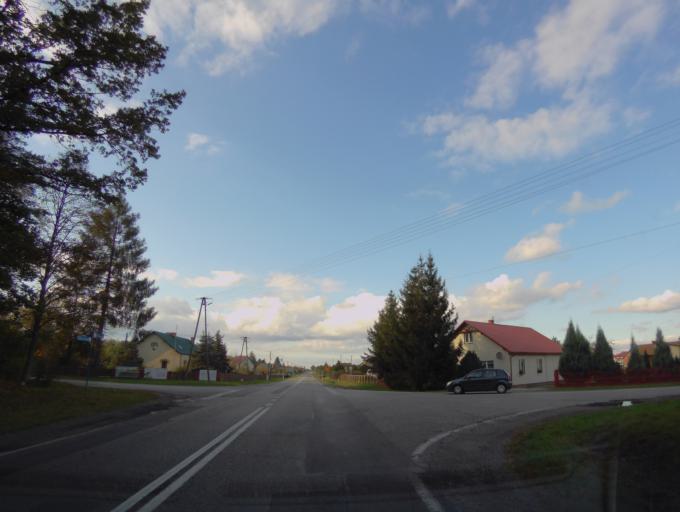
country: PL
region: Subcarpathian Voivodeship
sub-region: Powiat nizanski
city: Bieliny
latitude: 50.3981
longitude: 22.2966
